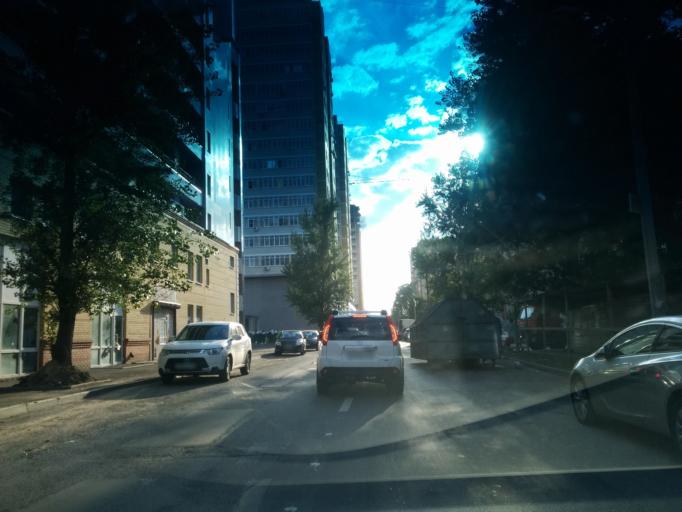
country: RU
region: Rostov
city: Severnyy
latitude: 47.2734
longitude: 39.7159
